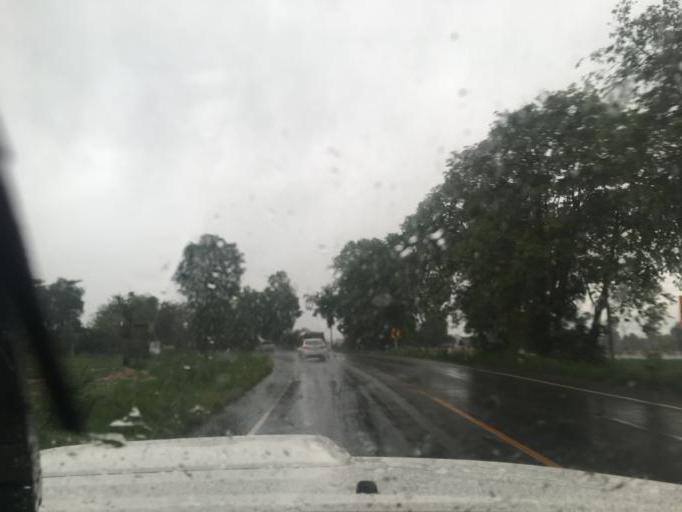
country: TH
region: Changwat Udon Thani
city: Udon Thani
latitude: 17.3012
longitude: 102.7026
